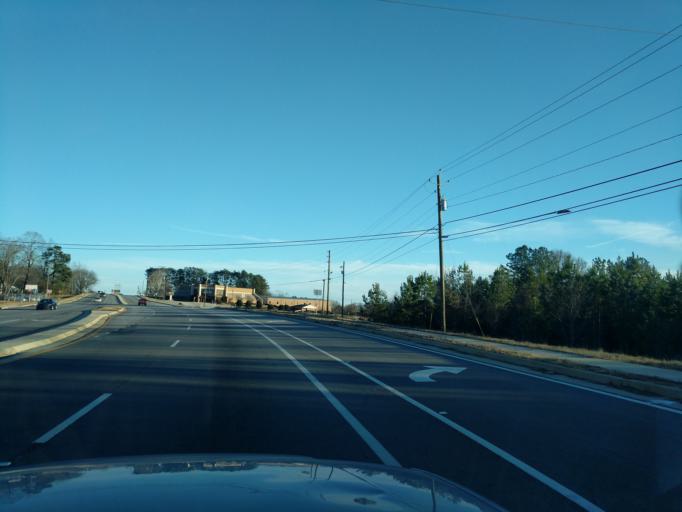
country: US
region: Georgia
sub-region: Stephens County
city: Toccoa
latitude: 34.5475
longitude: -83.2779
